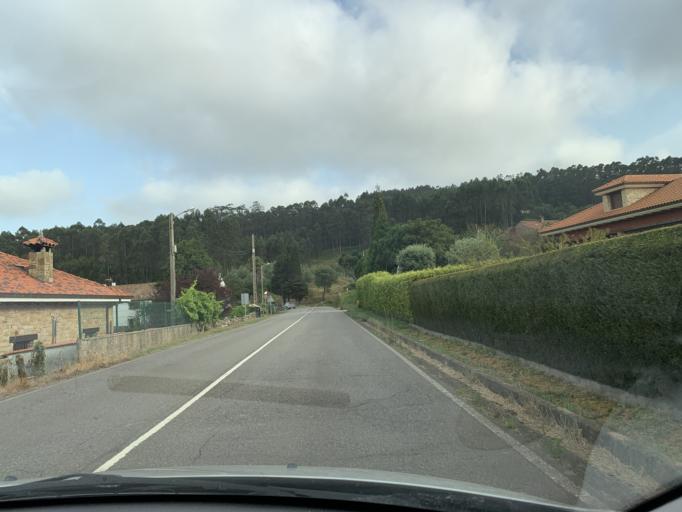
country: ES
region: Asturias
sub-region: Province of Asturias
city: Villaviciosa
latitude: 43.5193
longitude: -5.4388
